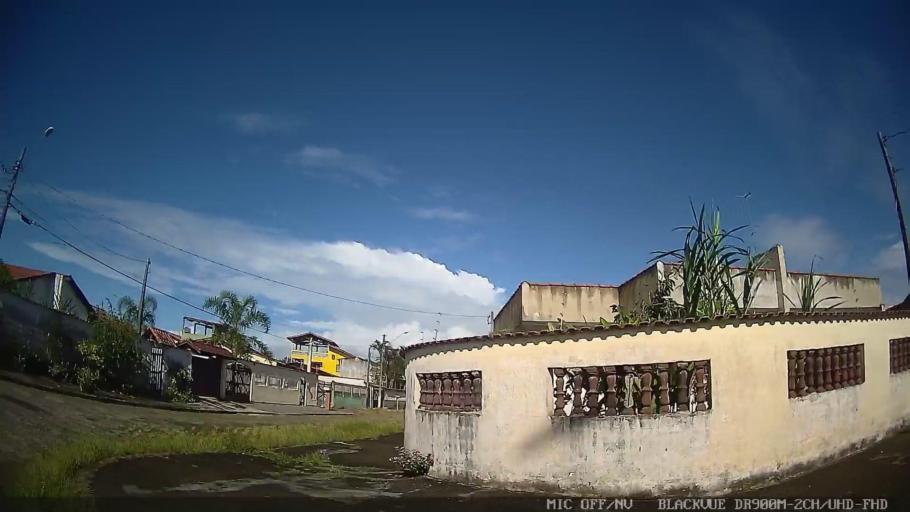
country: BR
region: Sao Paulo
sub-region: Itanhaem
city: Itanhaem
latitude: -24.2376
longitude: -46.8813
